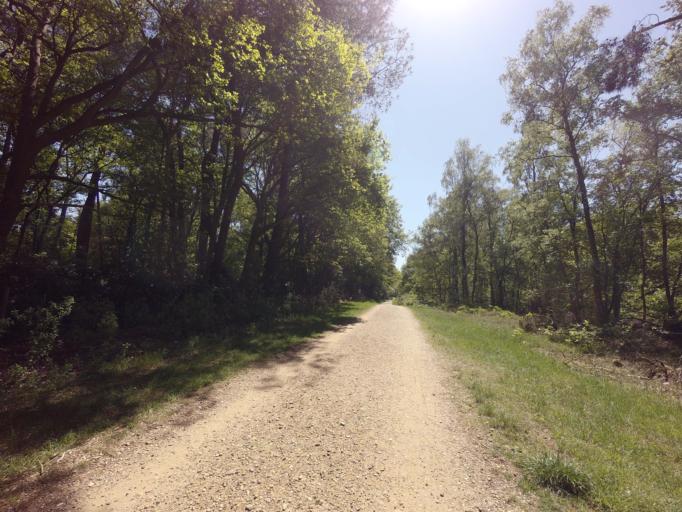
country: BE
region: Flanders
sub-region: Provincie Antwerpen
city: Kalmthout
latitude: 51.3850
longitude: 4.4497
